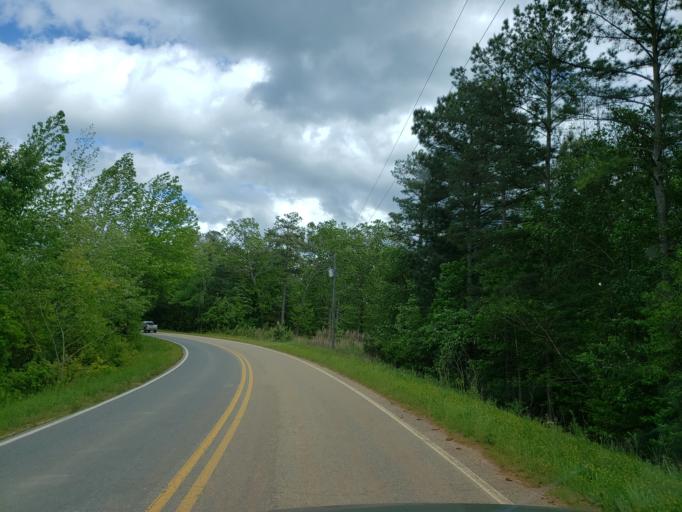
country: US
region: Georgia
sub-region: Haralson County
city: Tallapoosa
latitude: 33.6967
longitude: -85.3337
